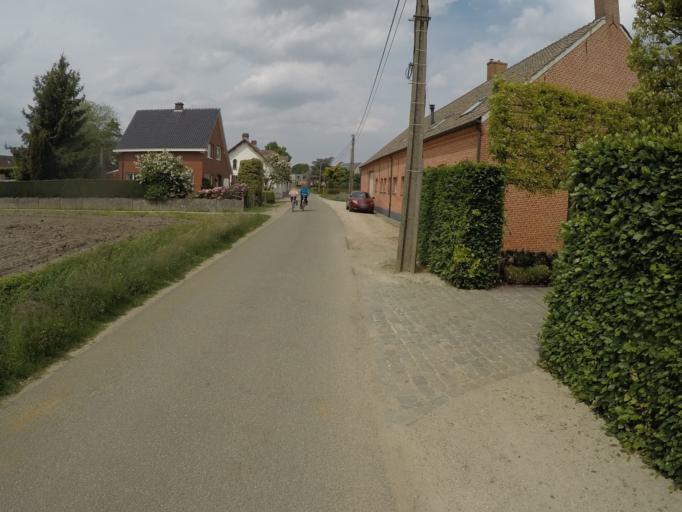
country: BE
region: Flanders
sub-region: Provincie Antwerpen
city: Zoersel
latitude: 51.2692
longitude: 4.7184
